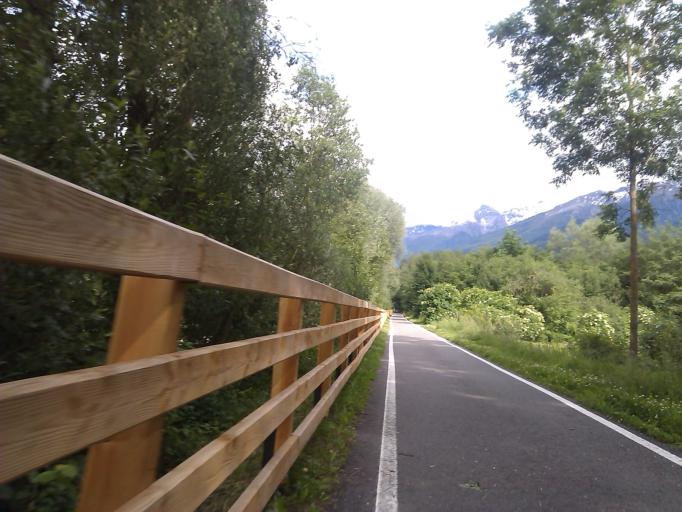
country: IT
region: Trentino-Alto Adige
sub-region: Bolzano
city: Sluderno
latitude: 46.6450
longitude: 10.5813
